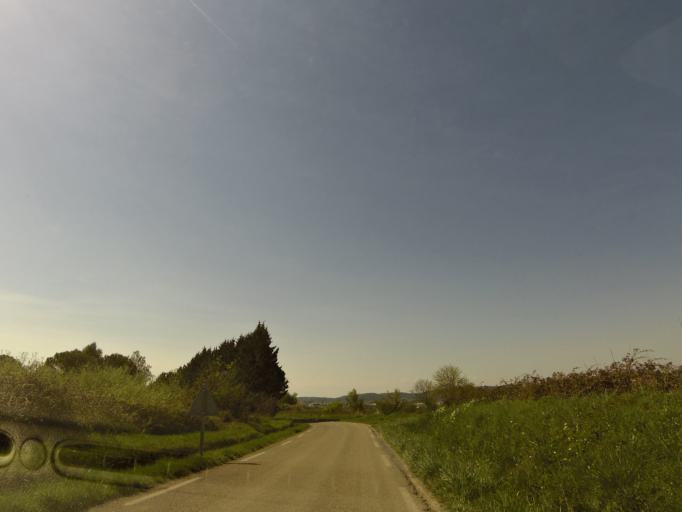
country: FR
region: Languedoc-Roussillon
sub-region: Departement du Gard
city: Nages-et-Solorgues
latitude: 43.7761
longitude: 4.2289
